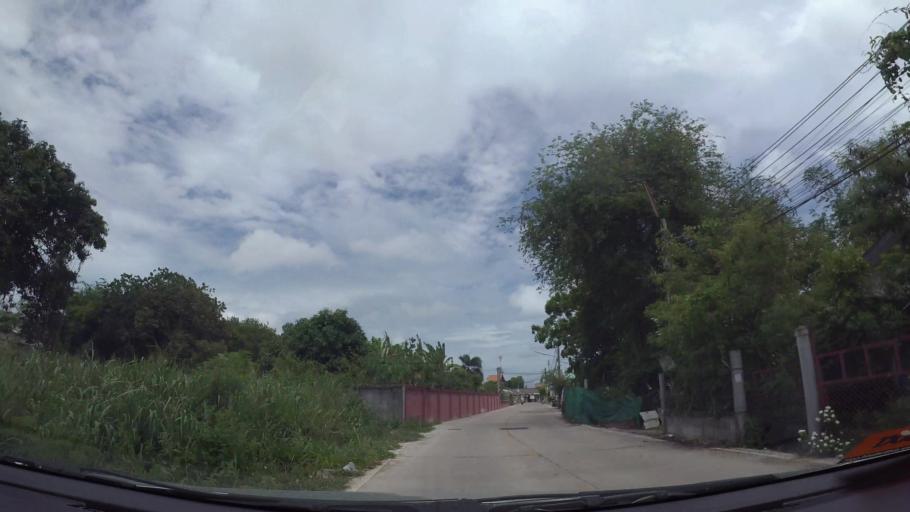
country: TH
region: Chon Buri
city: Sattahip
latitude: 12.6773
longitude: 100.9014
